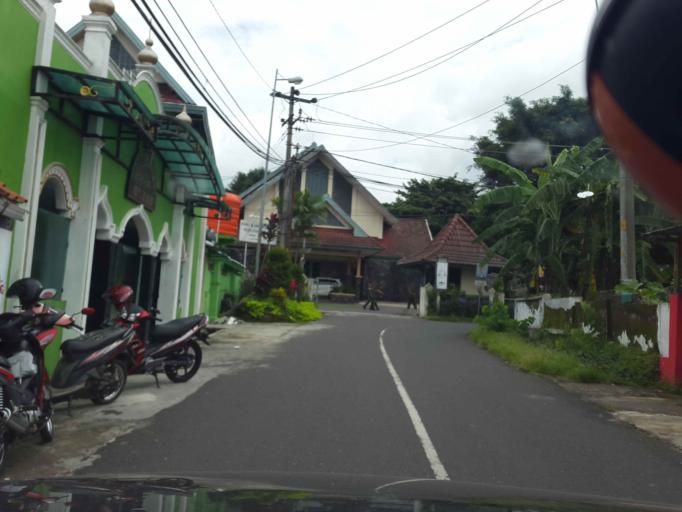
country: ID
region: Central Java
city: Salatiga
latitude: -7.3231
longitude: 110.5023
